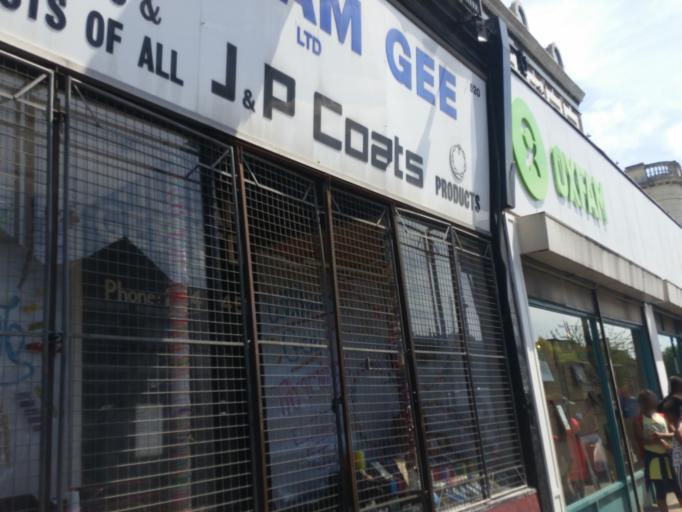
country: GB
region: England
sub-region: Greater London
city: Bethnal Green
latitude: 51.5444
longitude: -0.0760
